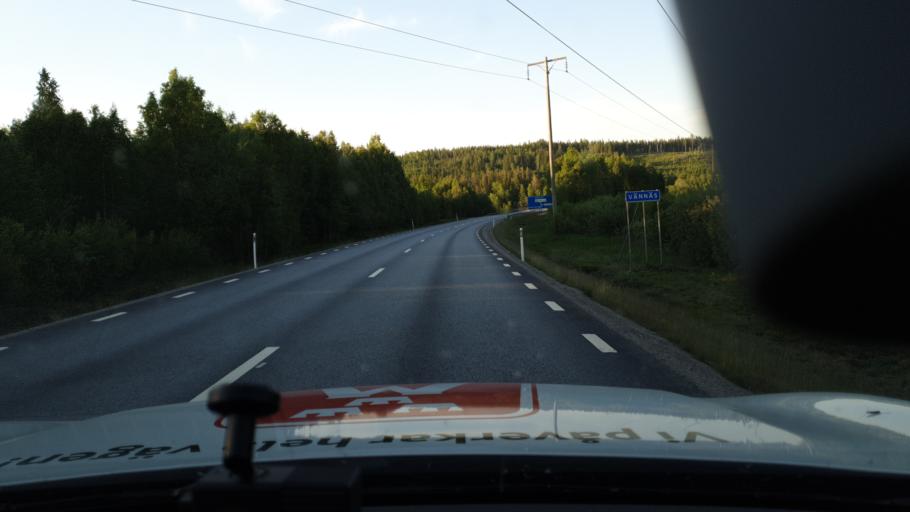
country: SE
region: Vaesterbotten
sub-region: Vannas Kommun
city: Vaennaes
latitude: 63.9080
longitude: 19.7001
